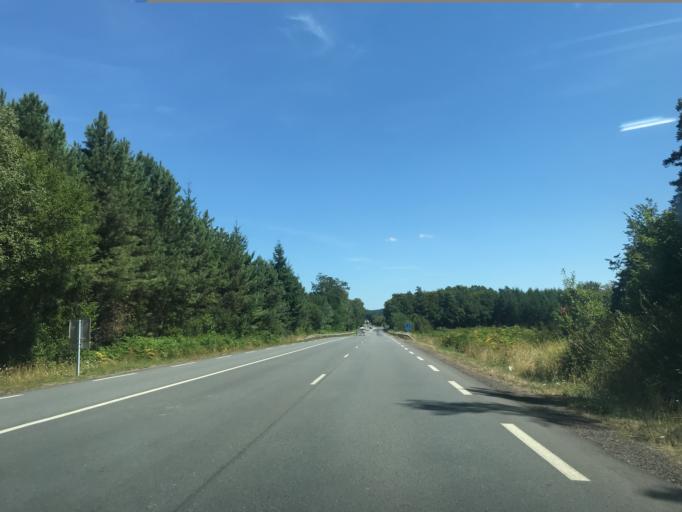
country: FR
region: Limousin
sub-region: Departement de la Correze
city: Correze
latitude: 45.3243
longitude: 1.8565
